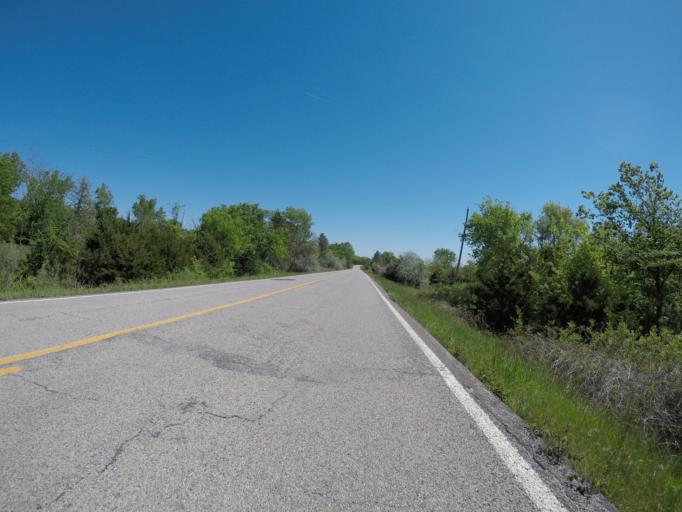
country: US
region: Kansas
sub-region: Osage County
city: Overbrook
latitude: 38.8840
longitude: -95.5396
